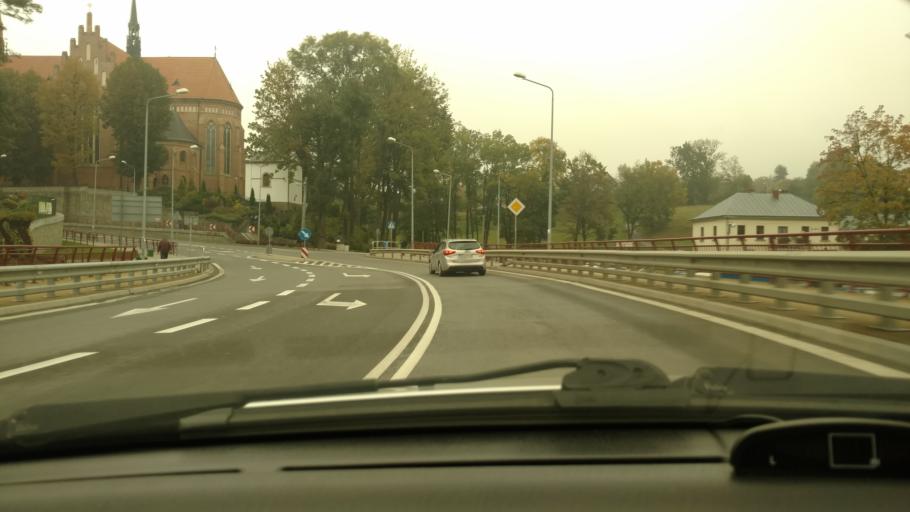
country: PL
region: Lesser Poland Voivodeship
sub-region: Powiat nowosadecki
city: Grybow
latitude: 49.6249
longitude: 20.9477
